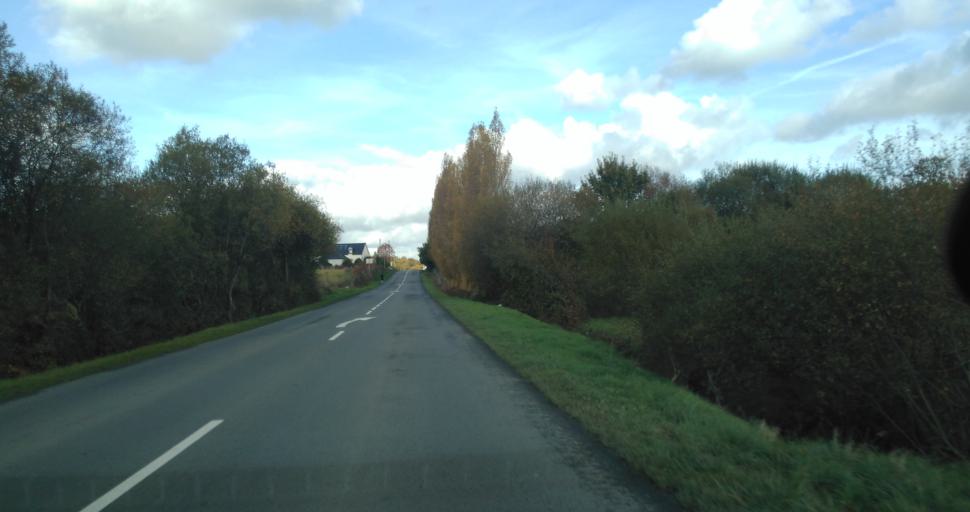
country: FR
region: Brittany
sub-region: Departement d'Ille-et-Vilaine
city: Boisgervilly
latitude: 48.1774
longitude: -2.0505
